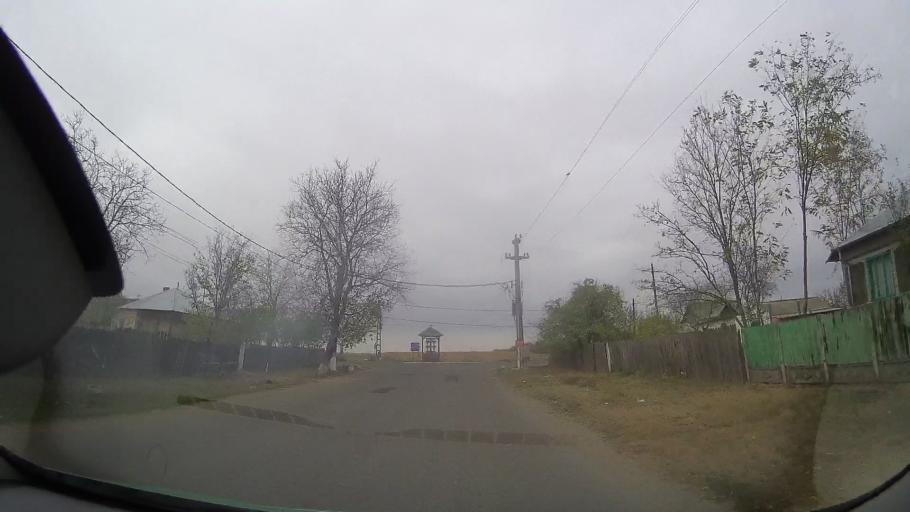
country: RO
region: Braila
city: Dudesti
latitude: 44.9425
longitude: 27.4246
